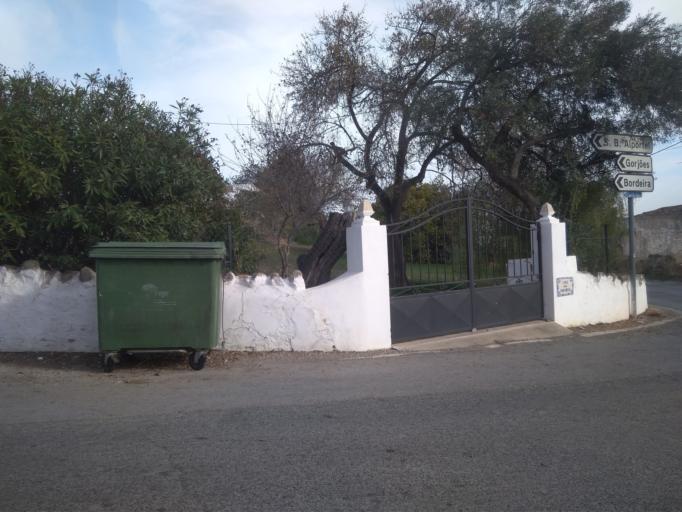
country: PT
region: Faro
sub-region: Faro
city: Santa Barbara de Nexe
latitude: 37.0997
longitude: -7.9612
